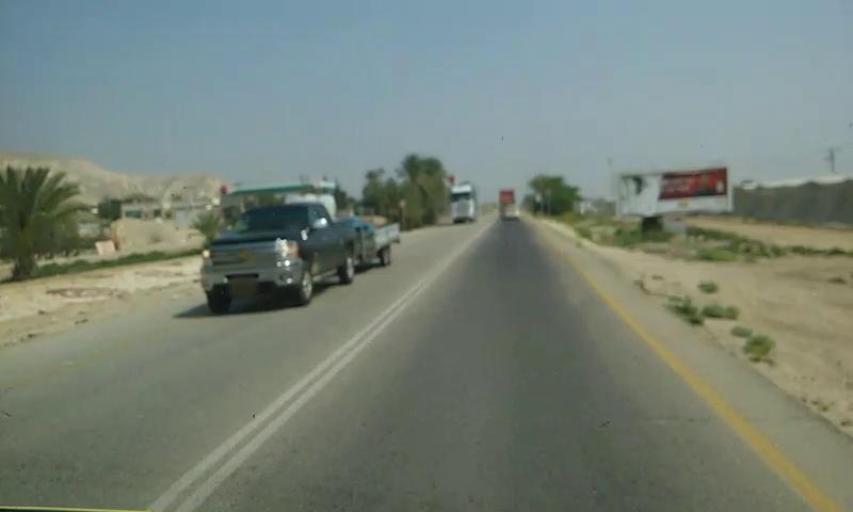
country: PS
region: West Bank
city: Al Fasayil
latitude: 32.0544
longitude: 35.4695
